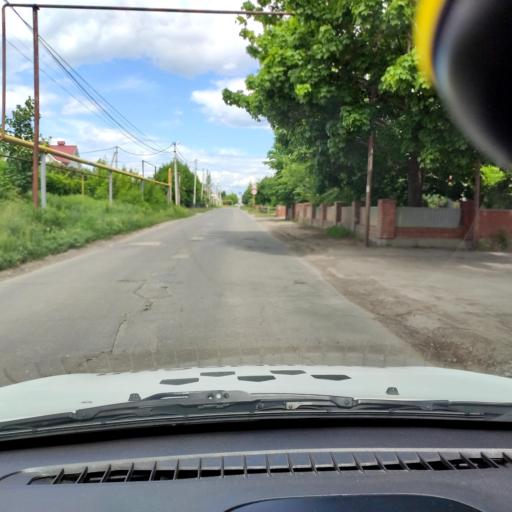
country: RU
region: Samara
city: Podstepki
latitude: 53.5164
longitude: 49.1628
